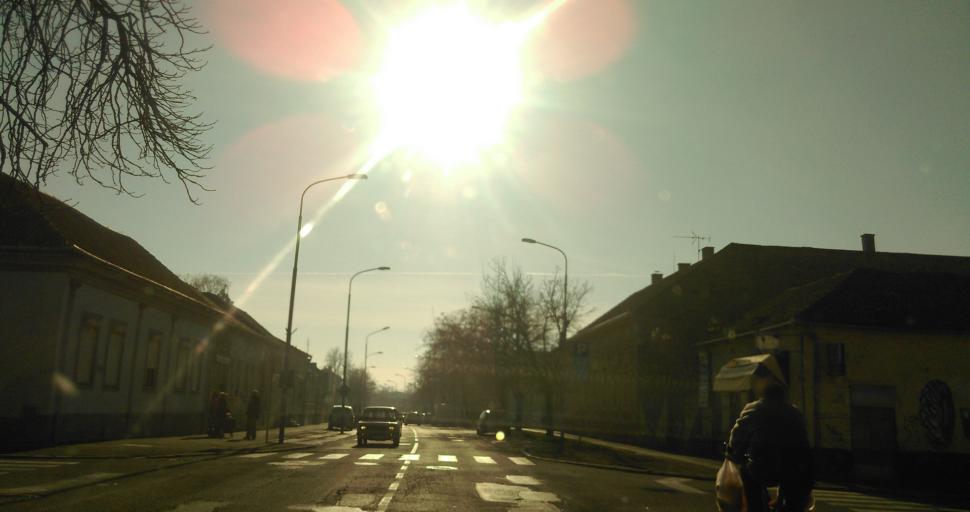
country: RS
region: Autonomna Pokrajina Vojvodina
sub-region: Sremski Okrug
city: Ruma
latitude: 45.0046
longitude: 19.8223
